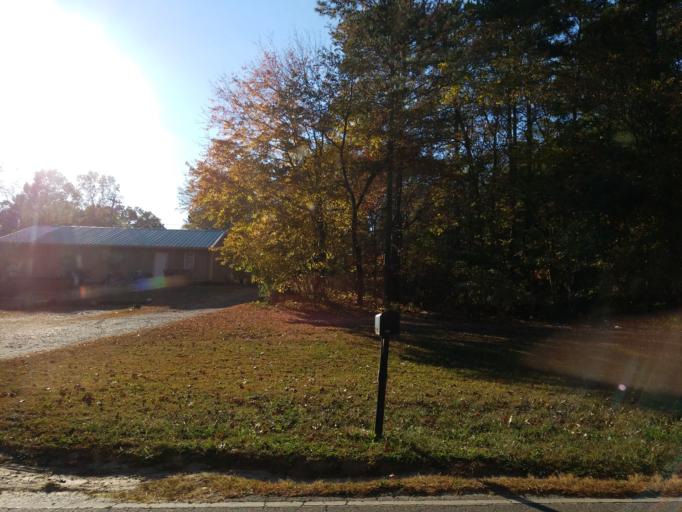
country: US
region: Georgia
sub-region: Gilmer County
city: Ellijay
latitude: 34.6077
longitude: -84.4643
